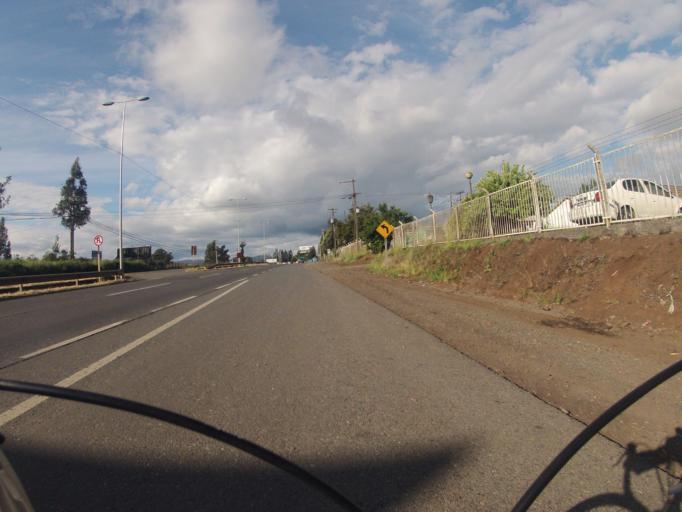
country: CL
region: Araucania
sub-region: Provincia de Cautin
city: Temuco
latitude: -38.7783
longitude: -72.6090
